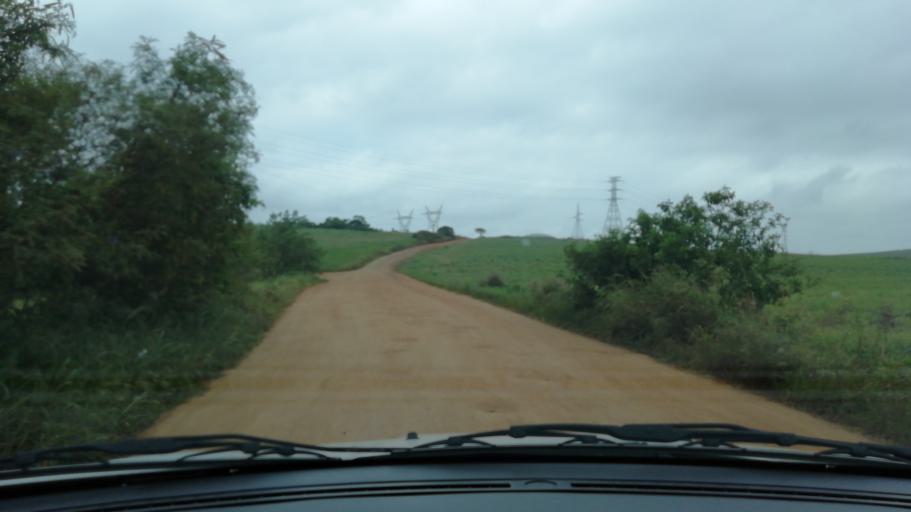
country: ZA
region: KwaZulu-Natal
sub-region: uThungulu District Municipality
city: Empangeni
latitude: -28.7334
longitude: 31.8993
